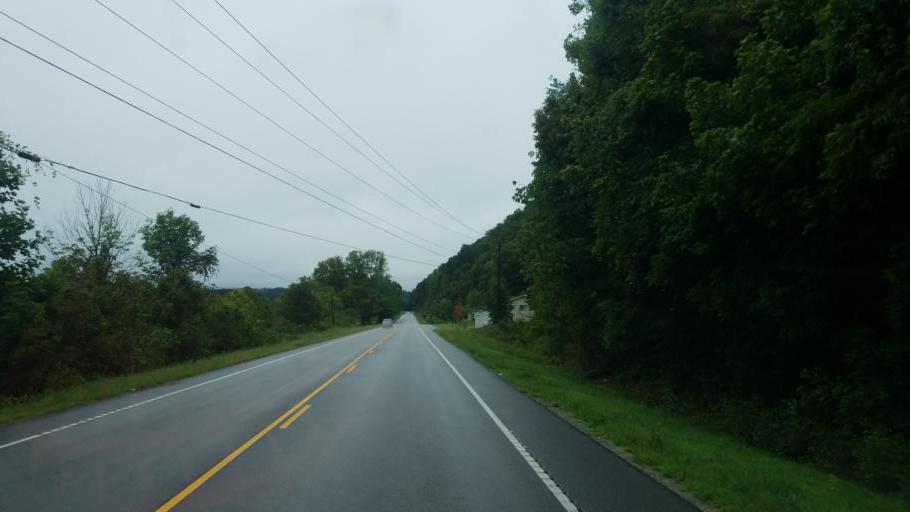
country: US
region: Ohio
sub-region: Adams County
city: Manchester
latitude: 38.6658
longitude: -83.6385
